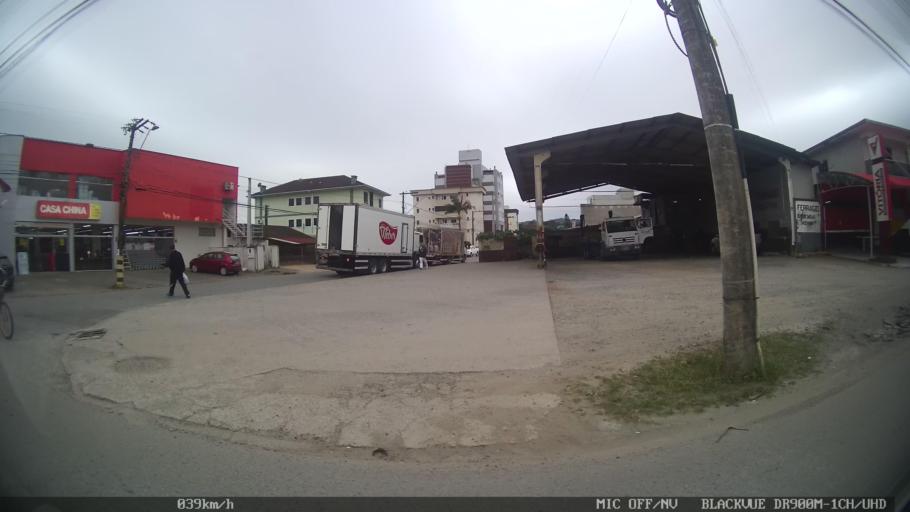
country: BR
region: Santa Catarina
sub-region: Joinville
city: Joinville
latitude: -26.2671
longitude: -48.8586
